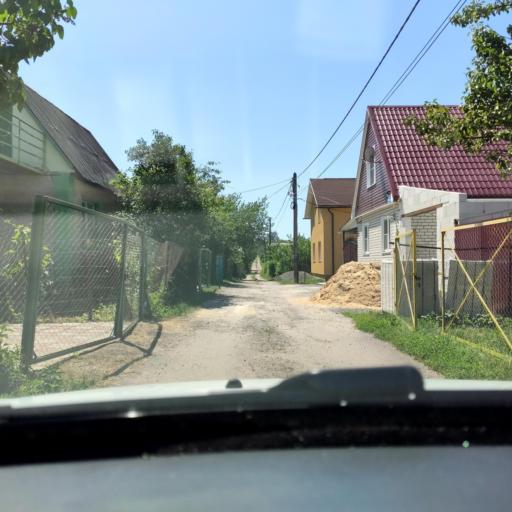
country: RU
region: Voronezj
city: Shilovo
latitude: 51.5901
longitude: 39.1497
